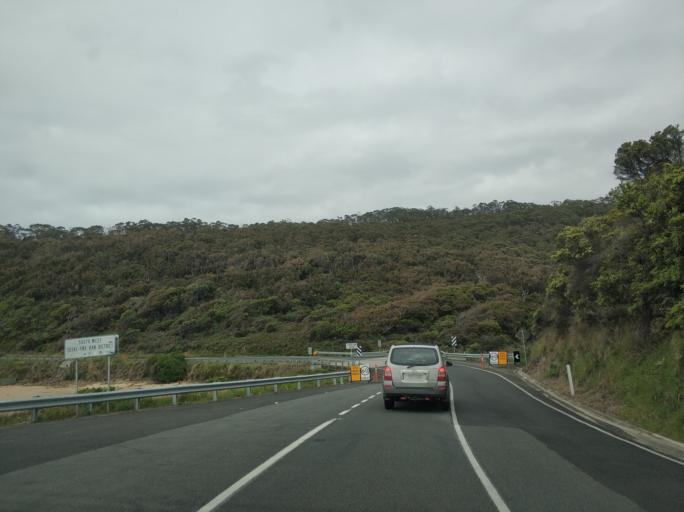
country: AU
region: Victoria
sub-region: Colac-Otway
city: Apollo Bay
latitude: -38.5960
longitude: 143.9198
